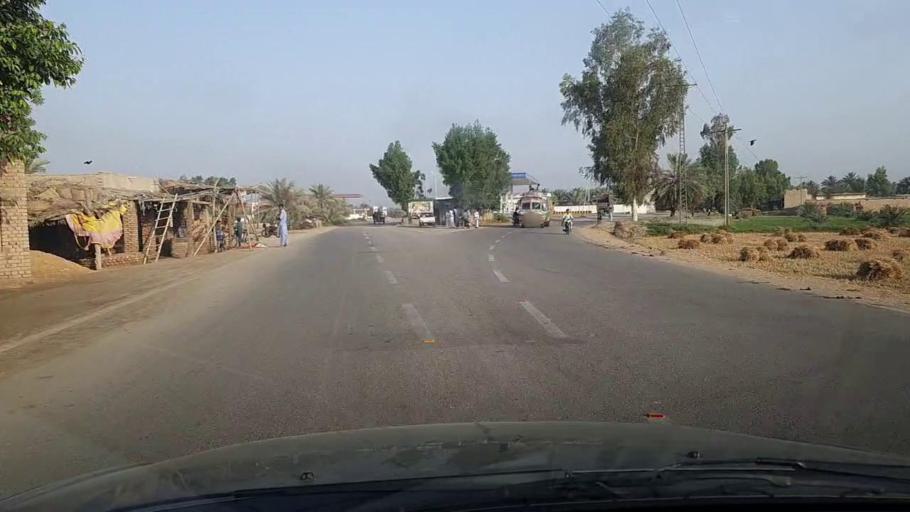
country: PK
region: Sindh
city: Khairpur
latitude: 27.5391
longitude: 68.7105
